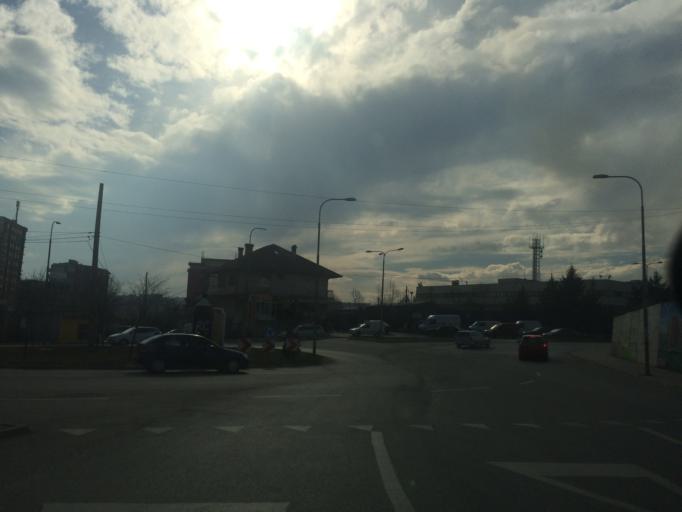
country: XK
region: Pristina
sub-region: Komuna e Prishtines
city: Pristina
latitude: 42.6458
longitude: 21.1697
